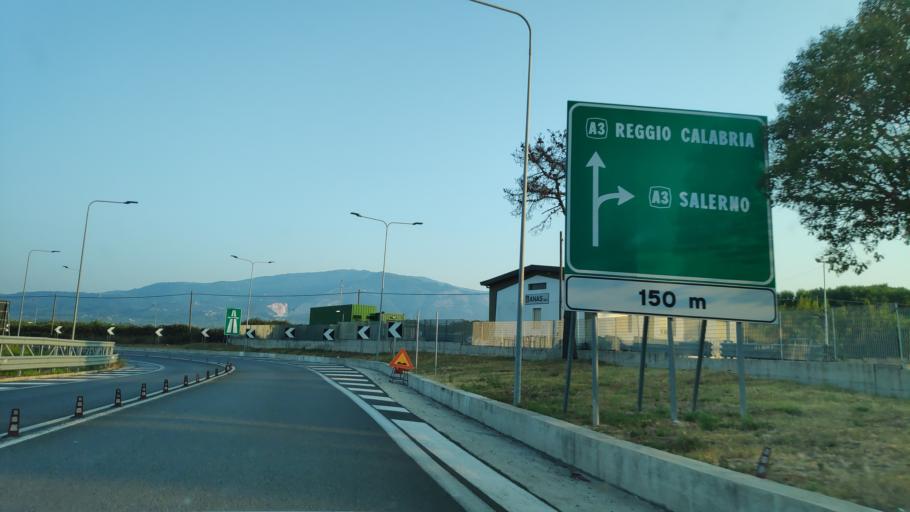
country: IT
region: Calabria
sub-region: Provincia di Catanzaro
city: Santa Eufemia Lamezia
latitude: 38.9183
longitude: 16.2671
